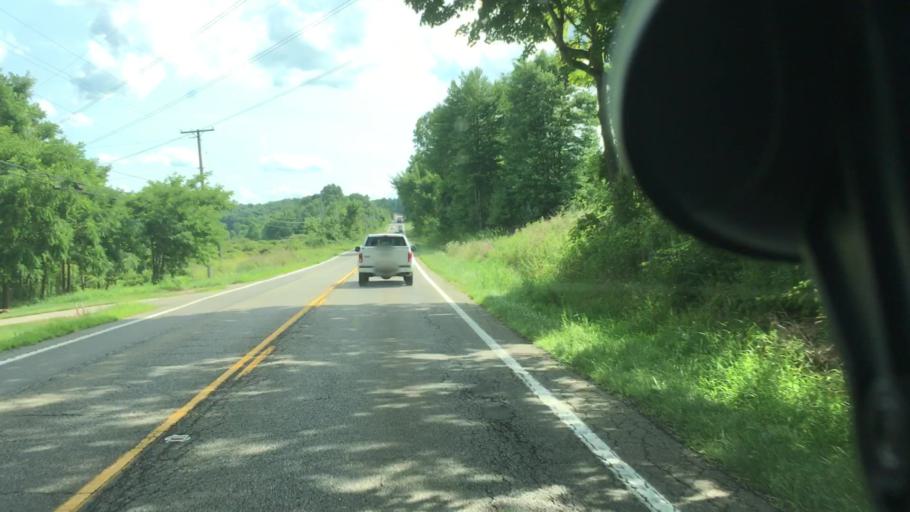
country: US
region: Ohio
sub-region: Columbiana County
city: Salem
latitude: 40.9522
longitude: -80.8334
